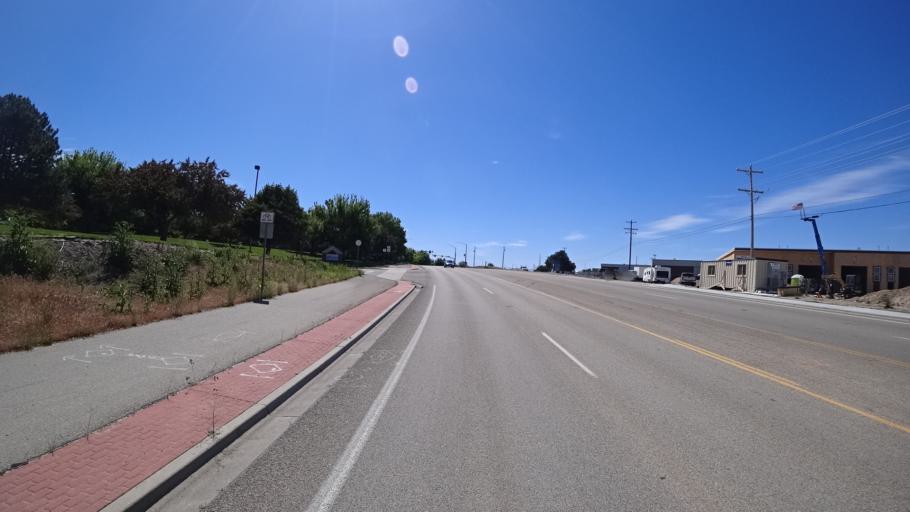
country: US
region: Idaho
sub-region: Ada County
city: Boise
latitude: 43.5448
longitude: -116.1575
